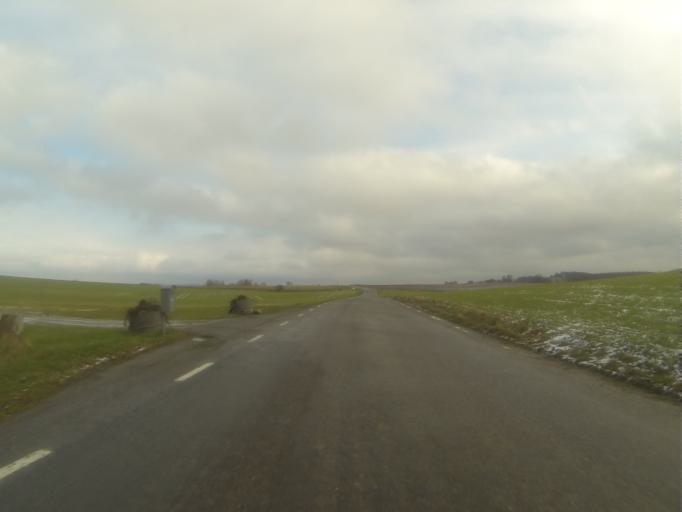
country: SE
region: Skane
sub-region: Svedala Kommun
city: Klagerup
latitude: 55.5935
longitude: 13.3083
